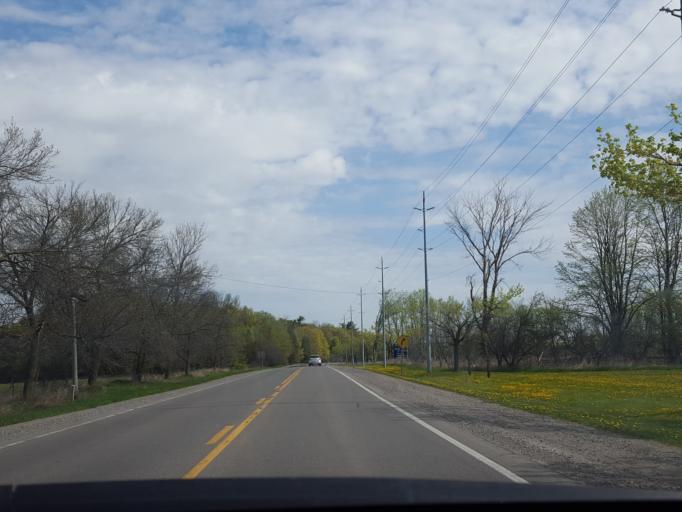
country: CA
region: Ontario
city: Uxbridge
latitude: 44.1745
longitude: -78.8933
